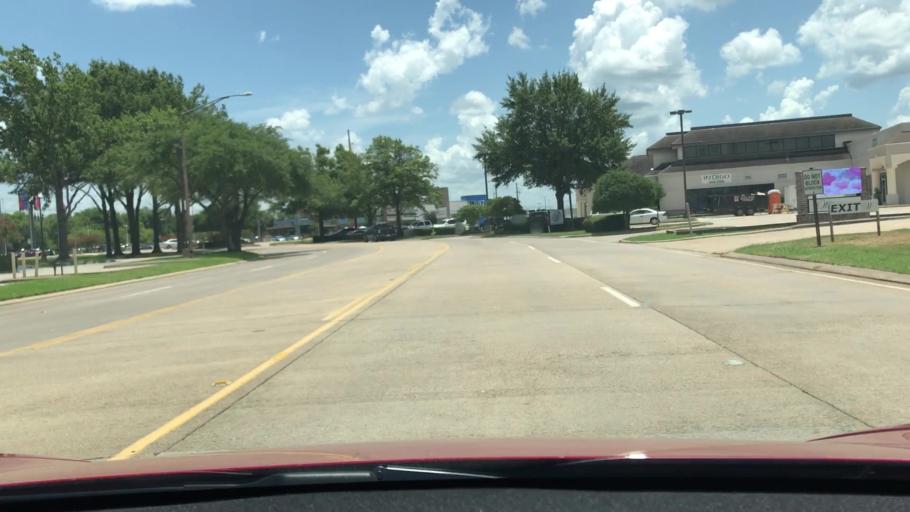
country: US
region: Louisiana
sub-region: Bossier Parish
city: Bossier City
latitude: 32.4242
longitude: -93.7215
